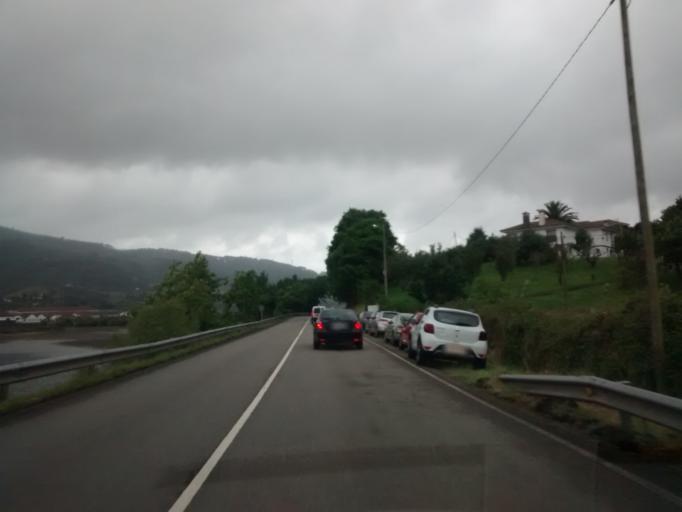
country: ES
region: Asturias
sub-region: Province of Asturias
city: Villaviciosa
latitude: 43.4996
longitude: -5.4267
